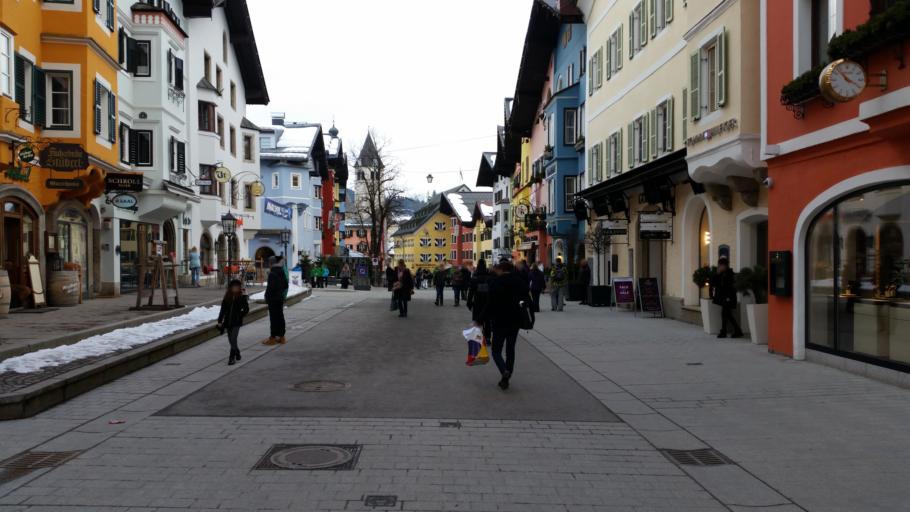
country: AT
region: Tyrol
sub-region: Politischer Bezirk Kitzbuhel
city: Kitzbuhel
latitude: 47.4463
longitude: 12.3913
